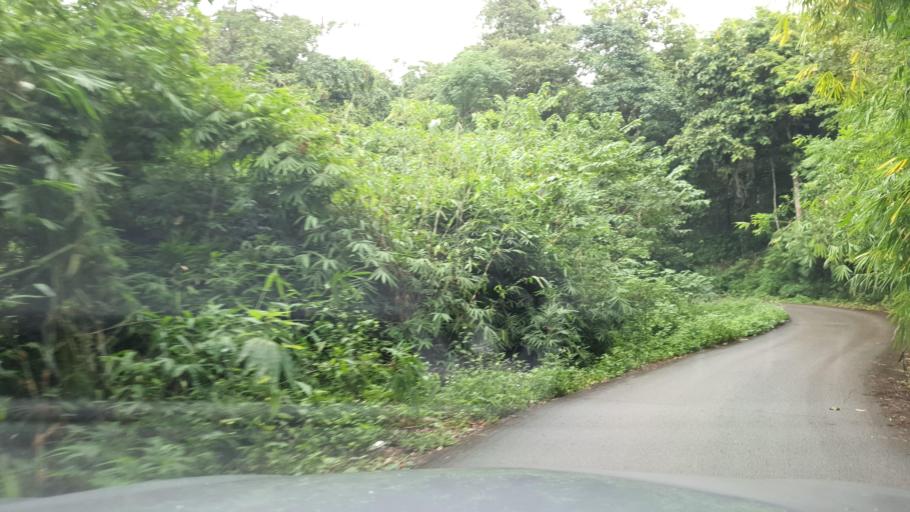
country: TH
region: Chiang Mai
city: Mae Taeng
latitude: 19.2041
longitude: 98.9343
